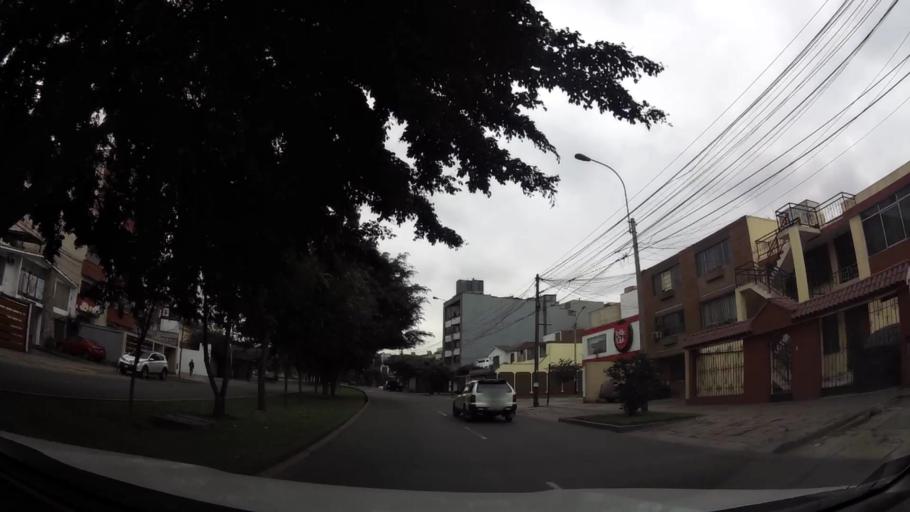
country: PE
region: Lima
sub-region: Lima
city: Surco
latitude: -12.1287
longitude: -76.9814
